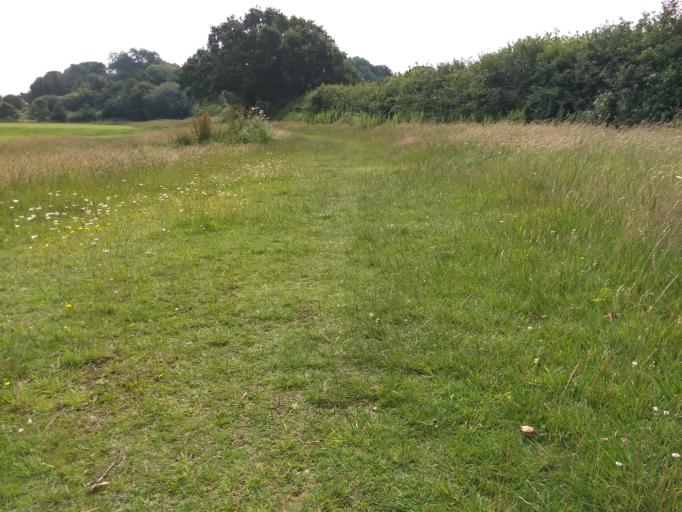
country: GB
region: England
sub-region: Isle of Wight
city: Ryde
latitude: 50.7167
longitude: -1.1829
